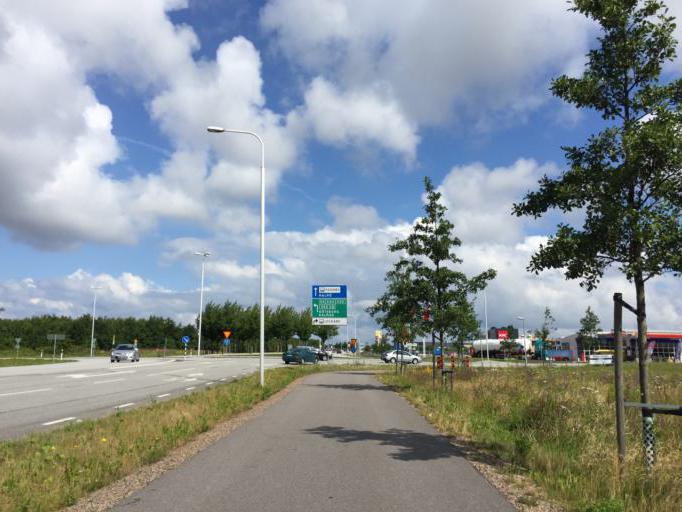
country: SE
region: Skane
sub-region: Malmo
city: Tygelsjo
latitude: 55.5475
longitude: 13.0331
